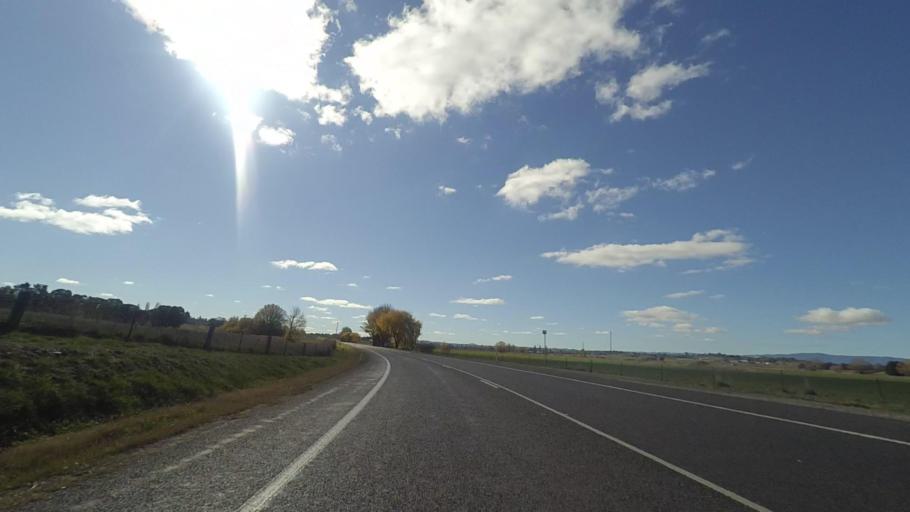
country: AU
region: New South Wales
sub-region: Bathurst Regional
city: Bathurst
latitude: -33.4509
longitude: 149.5788
